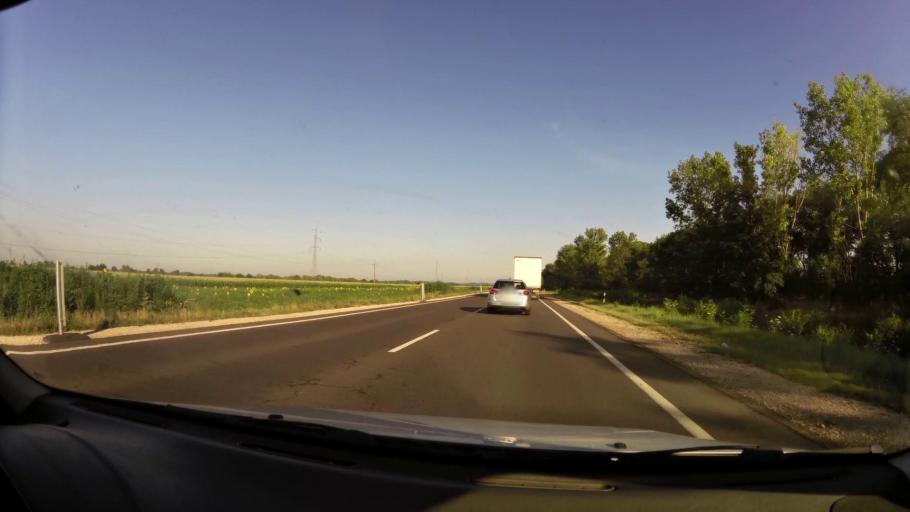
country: HU
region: Pest
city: Cegled
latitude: 47.2063
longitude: 19.7669
